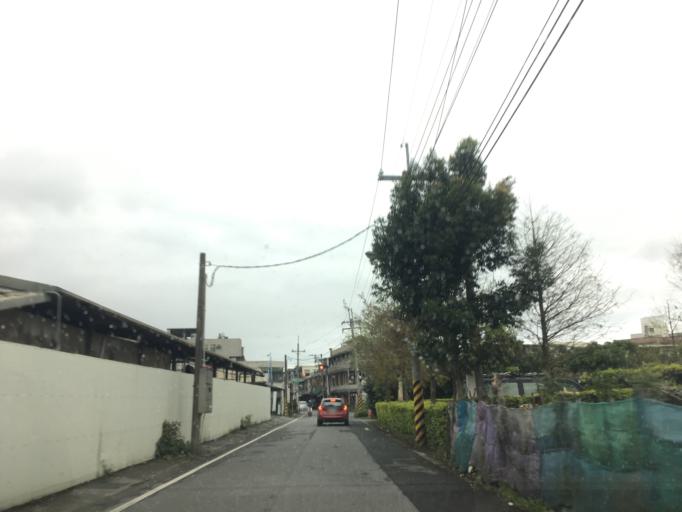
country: TW
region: Taiwan
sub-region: Hualien
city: Hualian
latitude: 23.9928
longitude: 121.5726
